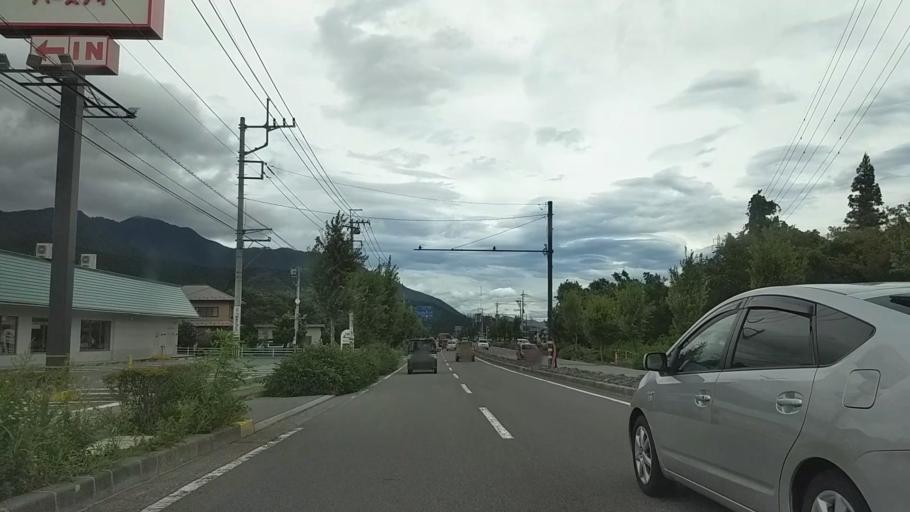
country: JP
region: Yamanashi
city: Fujikawaguchiko
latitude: 35.4892
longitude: 138.8132
